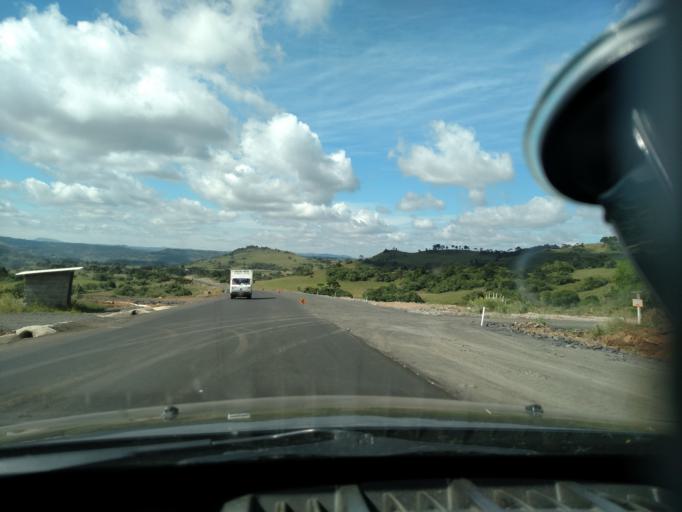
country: BR
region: Santa Catarina
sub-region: Sao Joaquim
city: Sao Joaquim
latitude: -28.0663
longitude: -50.0733
